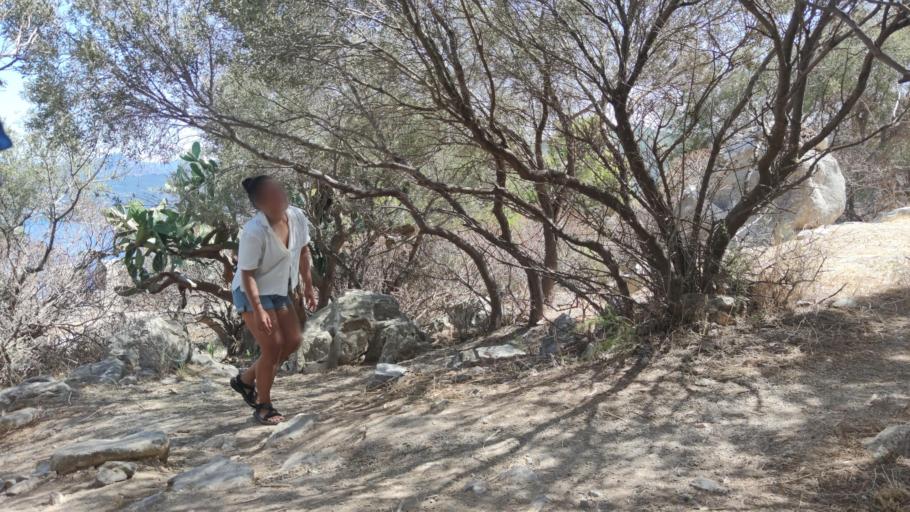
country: IT
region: Sicily
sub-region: Palermo
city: Cefalu
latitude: 38.0376
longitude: 14.0276
